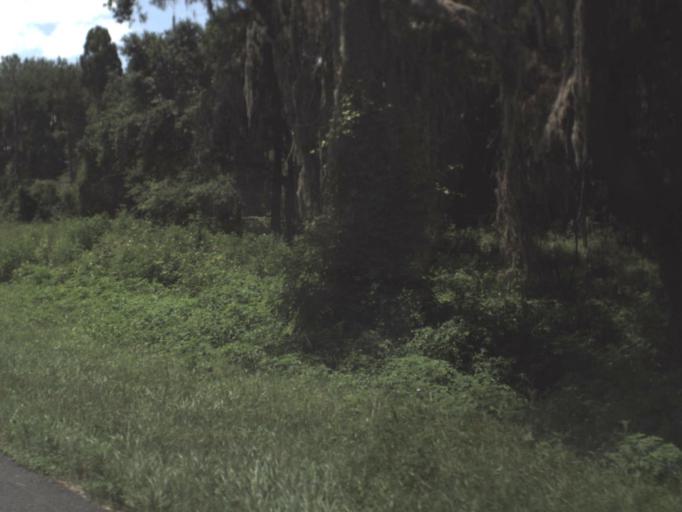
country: US
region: Florida
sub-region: Suwannee County
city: Wellborn
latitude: 30.3587
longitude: -82.7845
